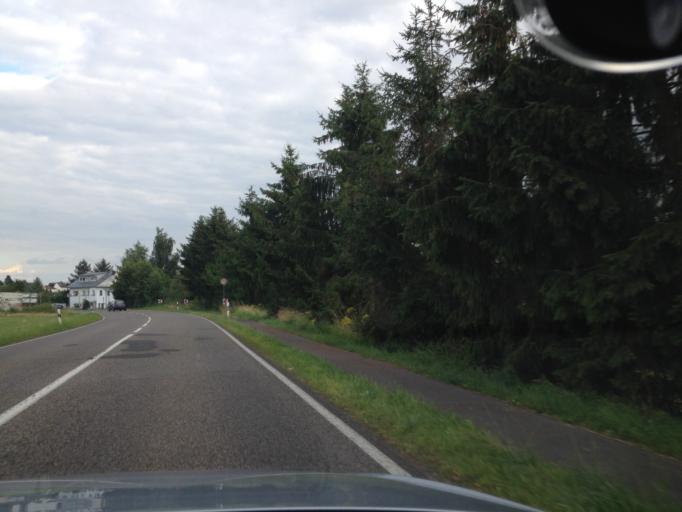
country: DE
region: Saarland
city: Illingen
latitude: 49.3794
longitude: 7.0824
